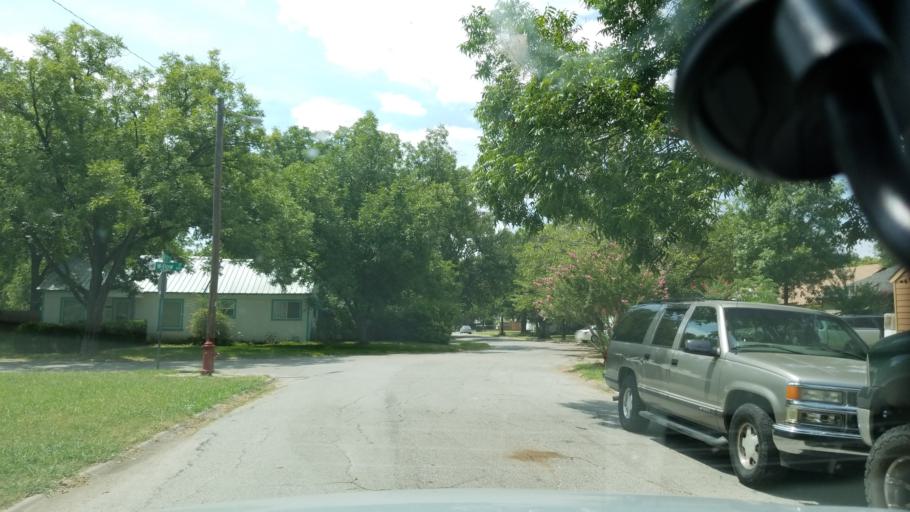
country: US
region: Texas
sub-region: Dallas County
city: Grand Prairie
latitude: 32.7537
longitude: -96.9906
